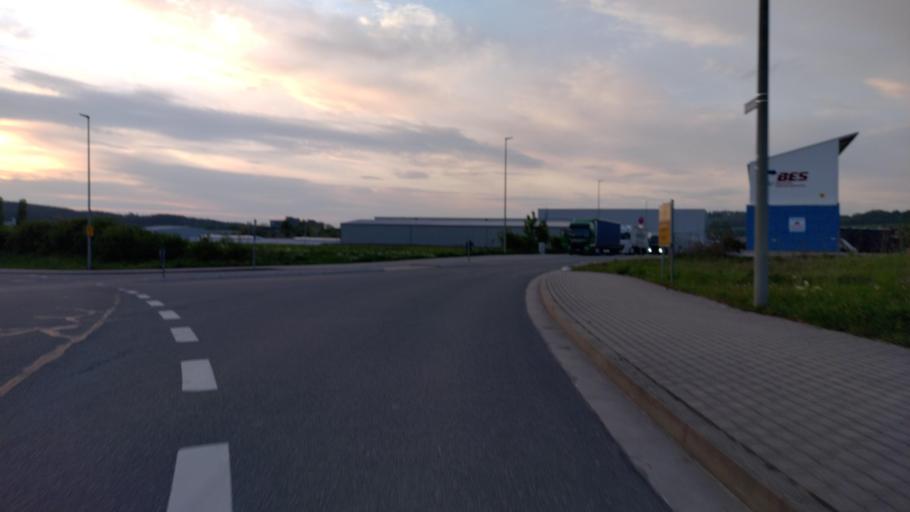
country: DE
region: Bavaria
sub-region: Upper Franconia
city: Bindlach
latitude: 49.9692
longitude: 11.6175
